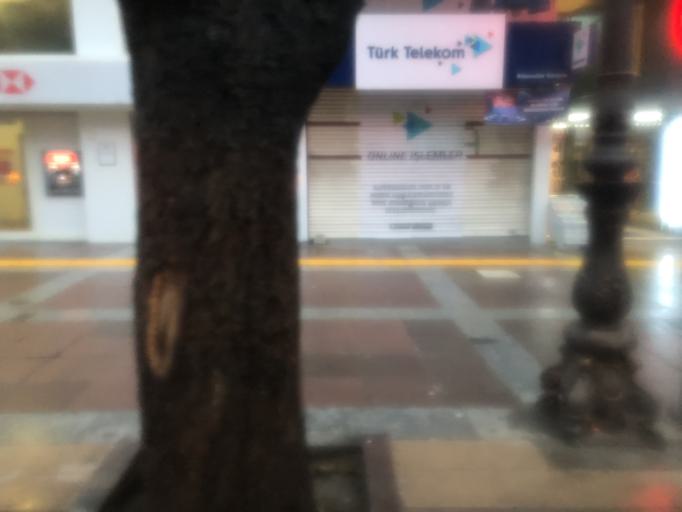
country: TR
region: Ankara
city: Ankara
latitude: 39.9240
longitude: 32.8545
